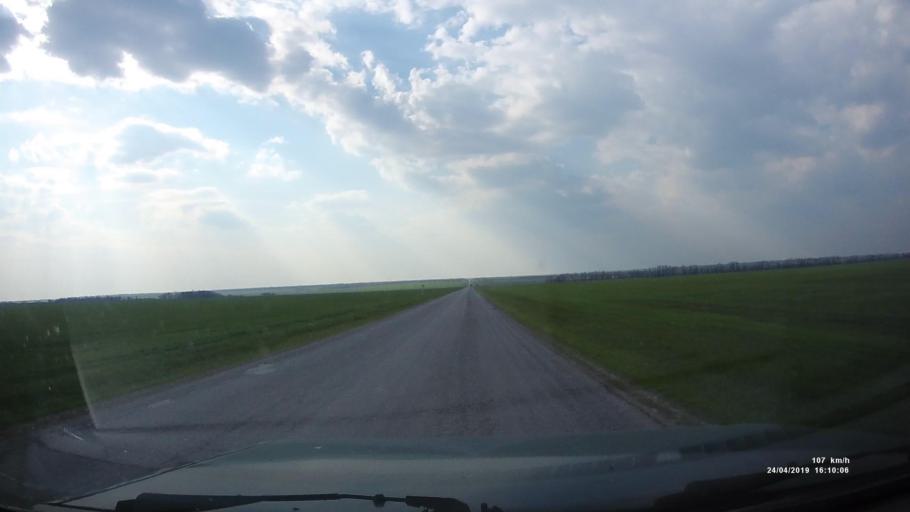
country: RU
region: Rostov
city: Sovetskoye
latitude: 46.7143
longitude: 42.2765
